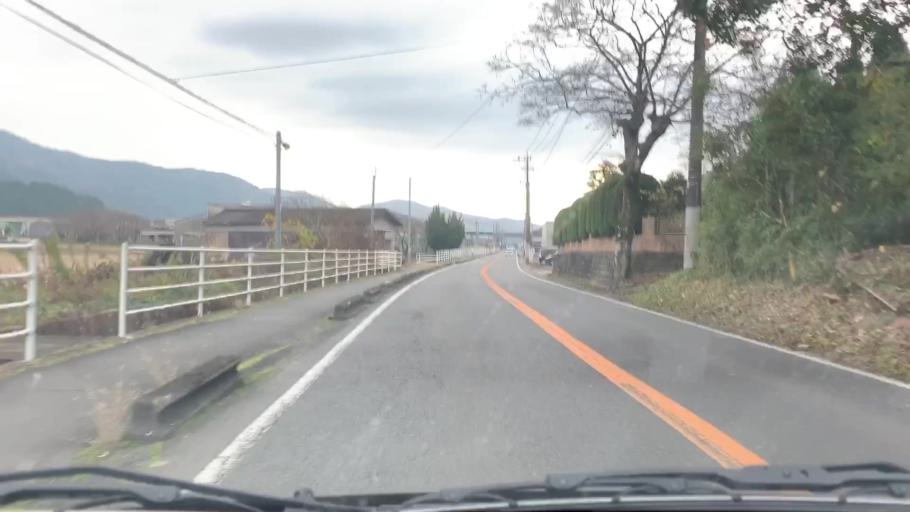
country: JP
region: Saga Prefecture
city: Takeocho-takeo
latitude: 33.1813
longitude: 130.0427
